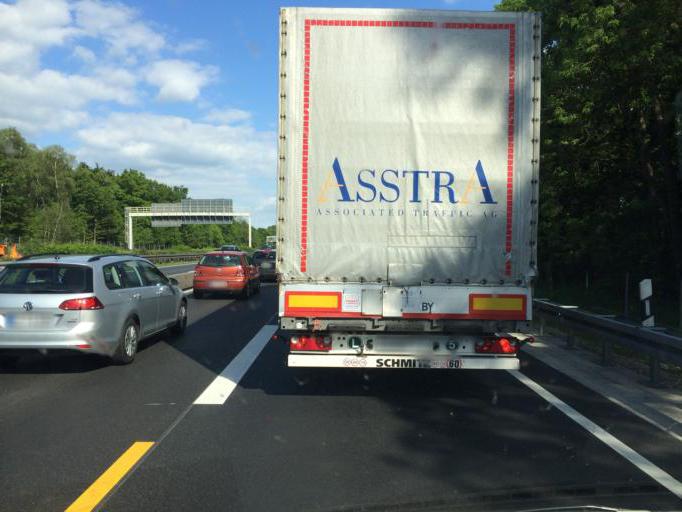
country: DE
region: Lower Saxony
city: Lehrte
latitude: 52.3952
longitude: 9.9166
